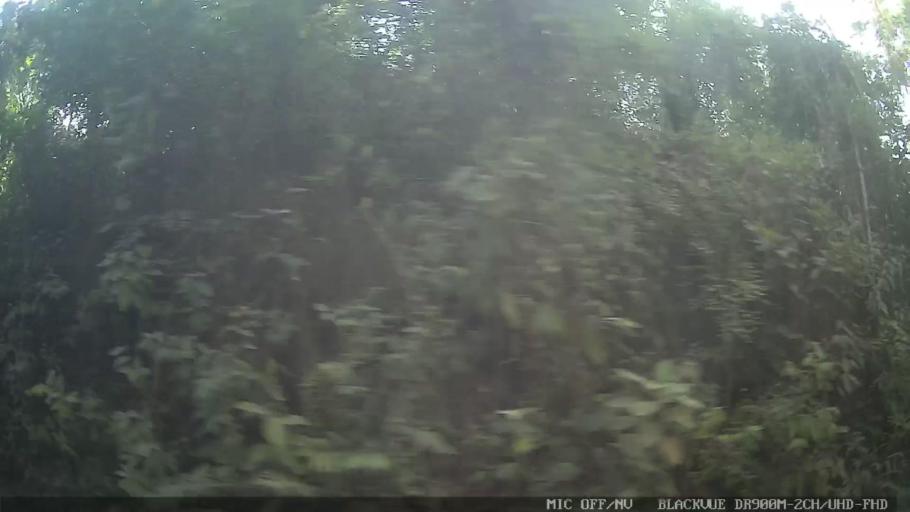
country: BR
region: Sao Paulo
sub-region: Bom Jesus Dos Perdoes
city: Bom Jesus dos Perdoes
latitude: -23.1446
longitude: -46.5087
